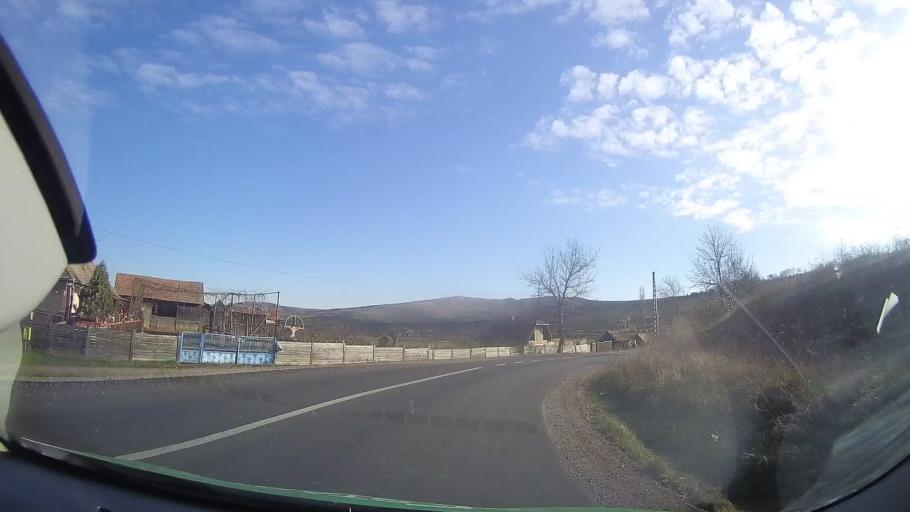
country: RO
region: Mures
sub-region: Comuna Iclanzel
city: Iclanzel
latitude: 46.5269
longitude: 24.2797
